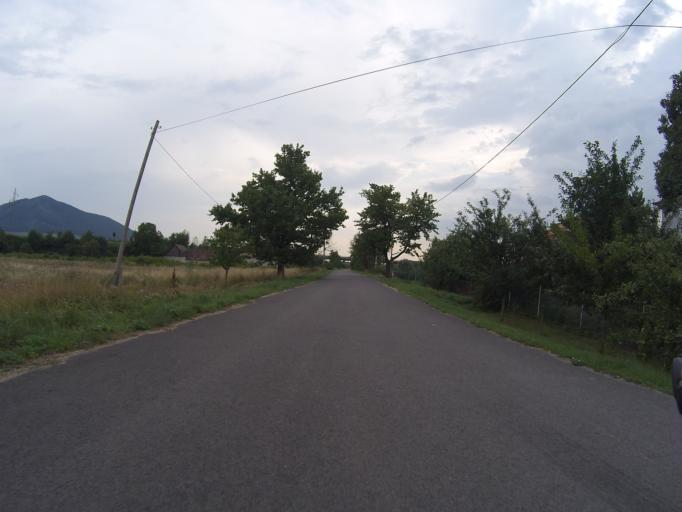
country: SK
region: Nitriansky
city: Puchov
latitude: 49.0479
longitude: 18.3020
